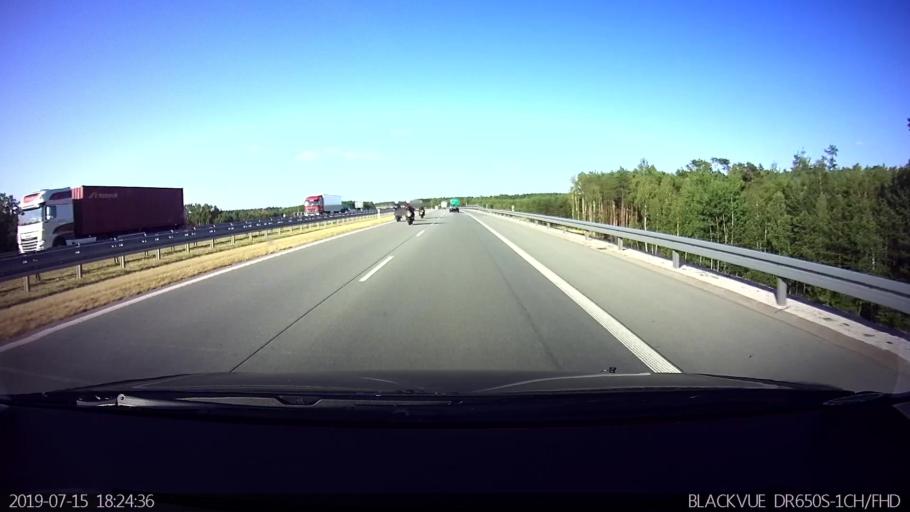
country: PL
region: Lodz Voivodeship
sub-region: Powiat laski
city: Lask
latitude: 51.5675
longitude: 19.1624
